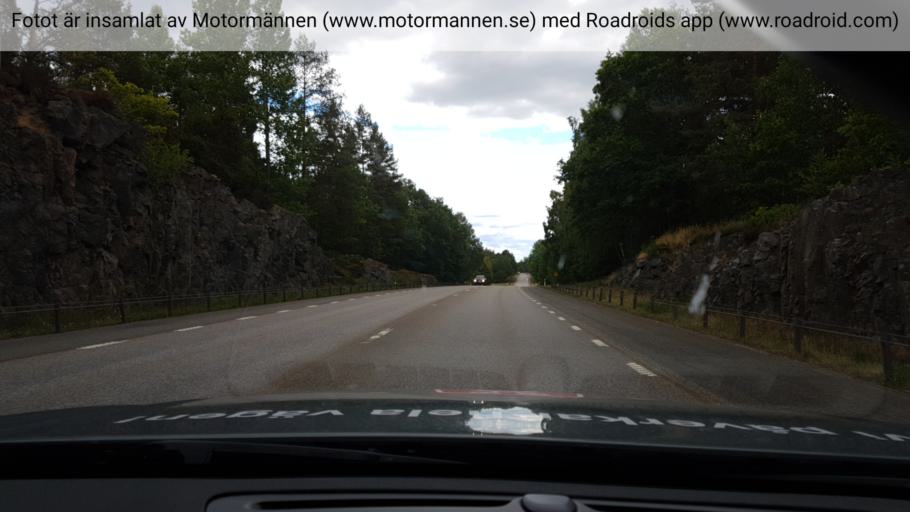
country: SE
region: Kalmar
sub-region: Vasterviks Kommun
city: Ankarsrum
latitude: 57.6764
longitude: 16.4437
